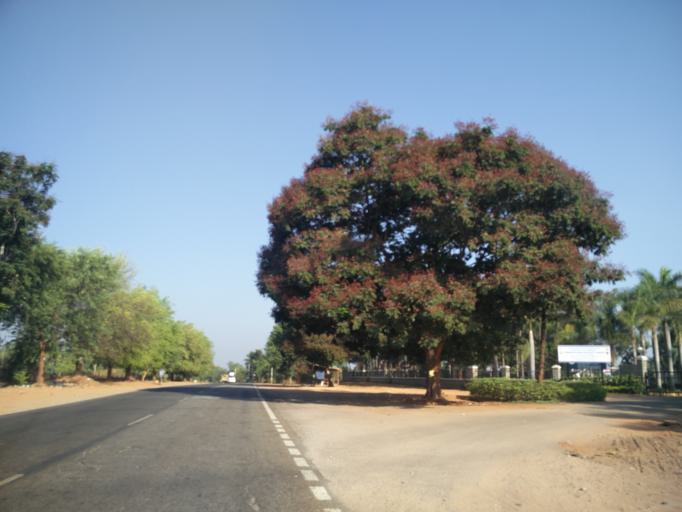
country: IN
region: Karnataka
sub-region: Tumkur
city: Gubbi
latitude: 13.3133
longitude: 76.9133
